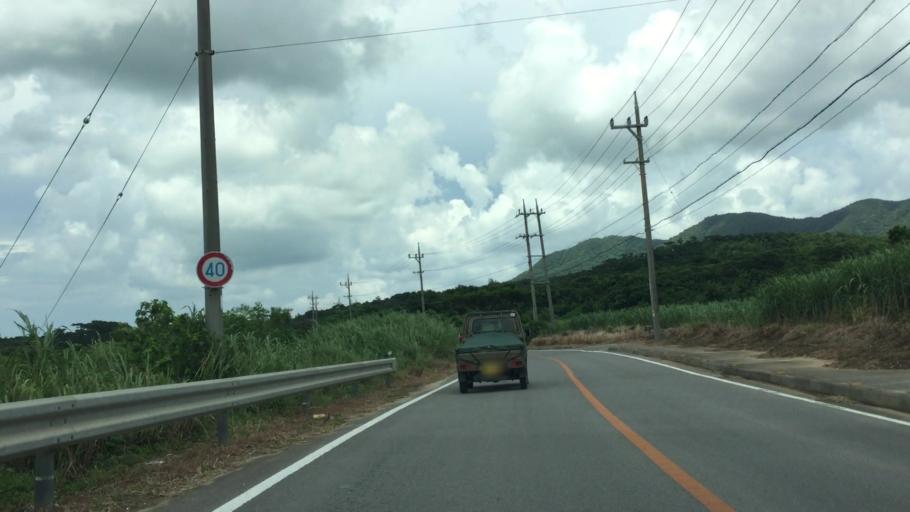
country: JP
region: Okinawa
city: Ishigaki
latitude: 24.3993
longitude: 124.1516
